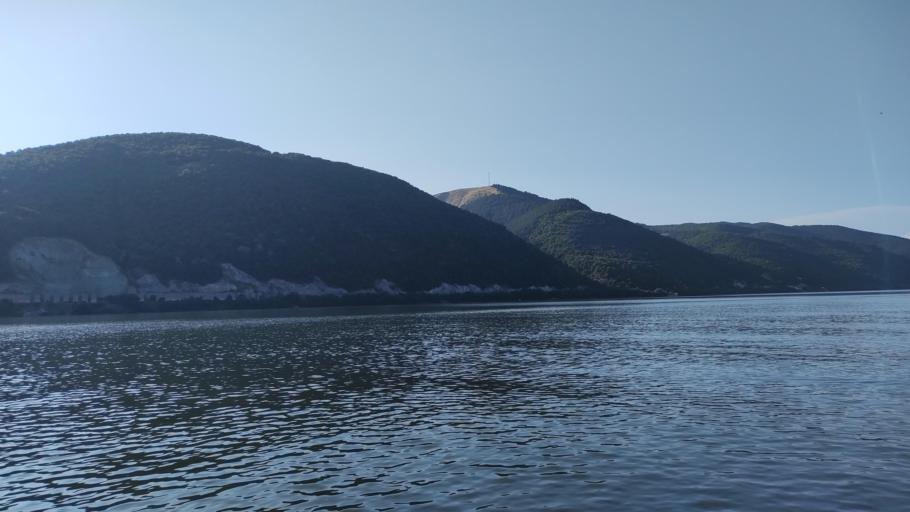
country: RO
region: Mehedinti
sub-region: Comuna Dubova
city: Dubova
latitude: 44.5425
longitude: 22.2209
